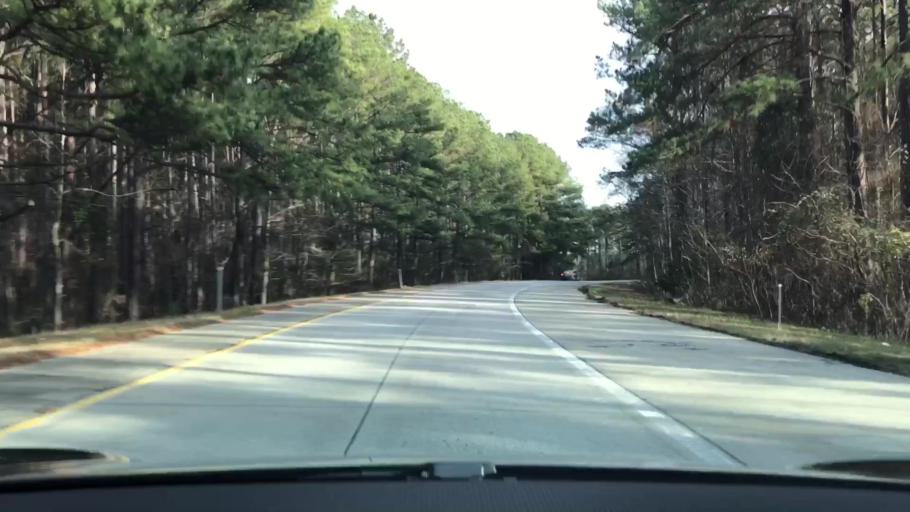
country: US
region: Georgia
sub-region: Taliaferro County
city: Crawfordville
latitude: 33.4980
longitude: -82.8078
